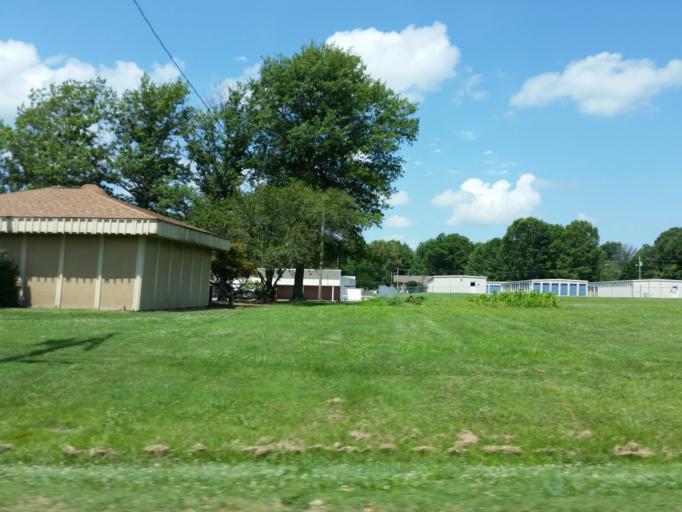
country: US
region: Tennessee
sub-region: Weakley County
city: Martin
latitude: 36.3670
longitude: -88.8503
